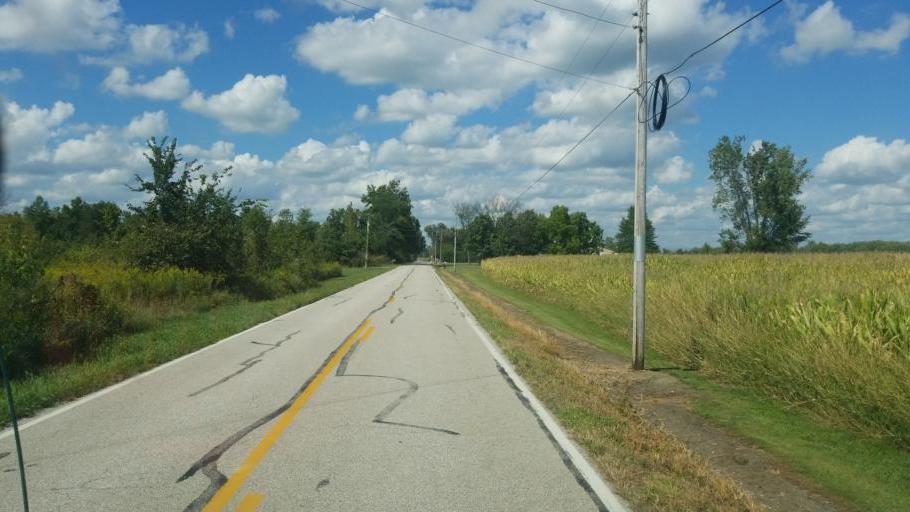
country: US
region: Ohio
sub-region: Union County
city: Richwood
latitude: 40.3267
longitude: -83.2377
